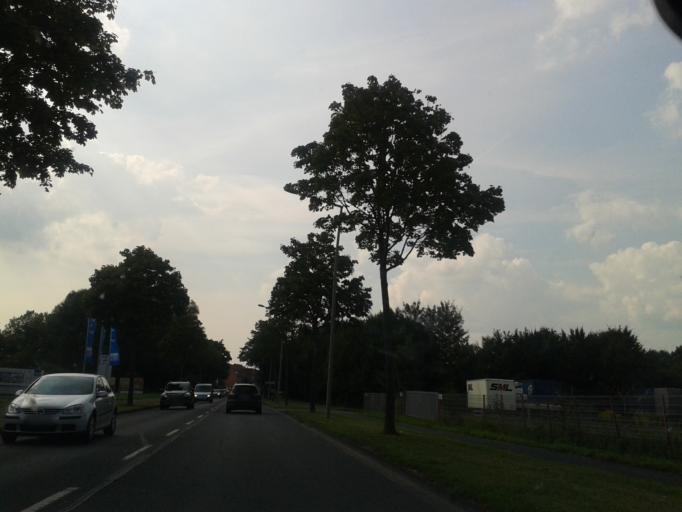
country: DE
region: North Rhine-Westphalia
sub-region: Regierungsbezirk Detmold
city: Paderborn
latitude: 51.7369
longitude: 8.7742
